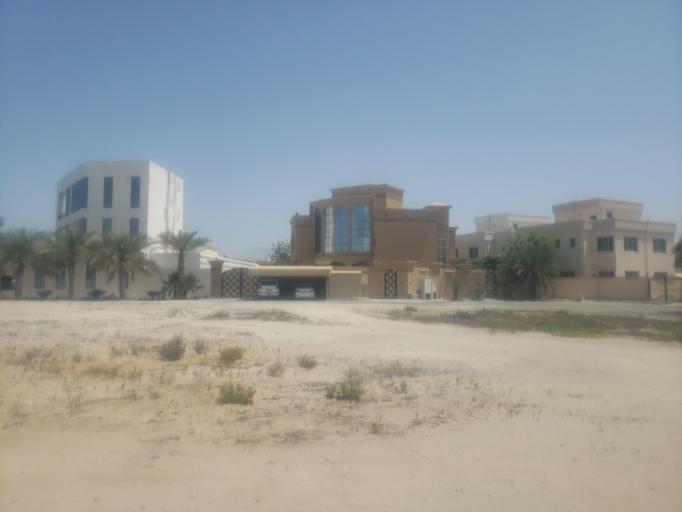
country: AE
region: Ra's al Khaymah
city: Ras al-Khaimah
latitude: 25.8103
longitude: 55.9555
